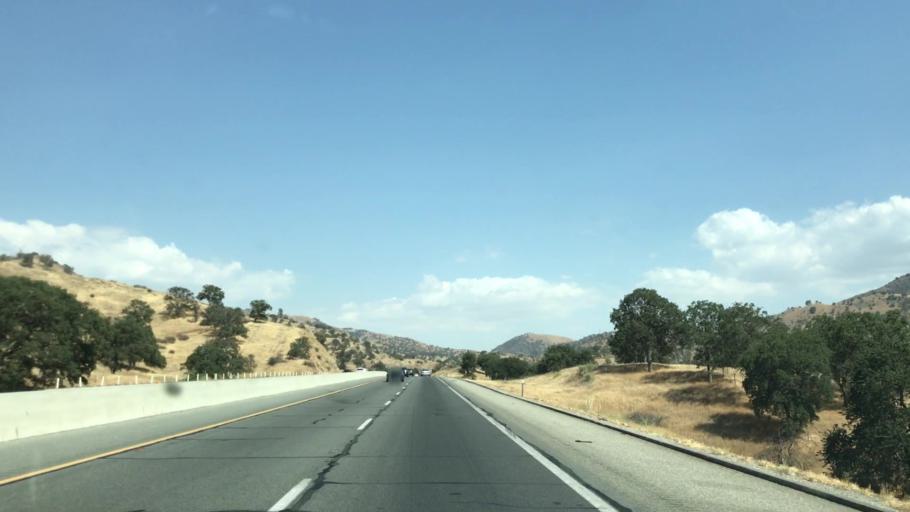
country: US
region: California
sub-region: Kern County
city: Golden Hills
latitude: 35.2105
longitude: -118.5432
